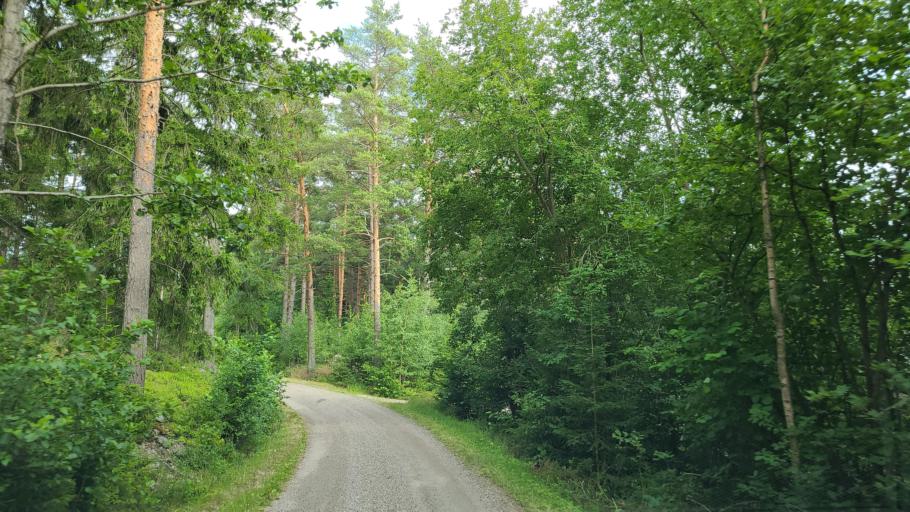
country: FI
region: Varsinais-Suomi
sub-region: Aboland-Turunmaa
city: Nagu
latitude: 60.1297
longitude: 21.8038
